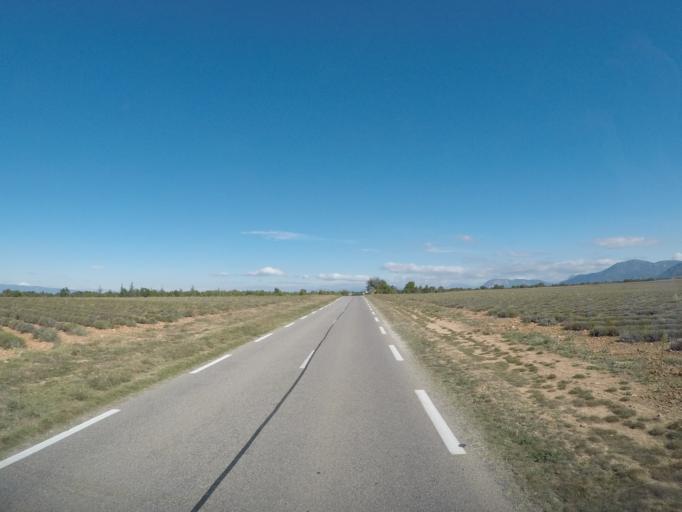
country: FR
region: Provence-Alpes-Cote d'Azur
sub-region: Departement des Alpes-de-Haute-Provence
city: Riez
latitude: 43.8822
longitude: 6.1318
